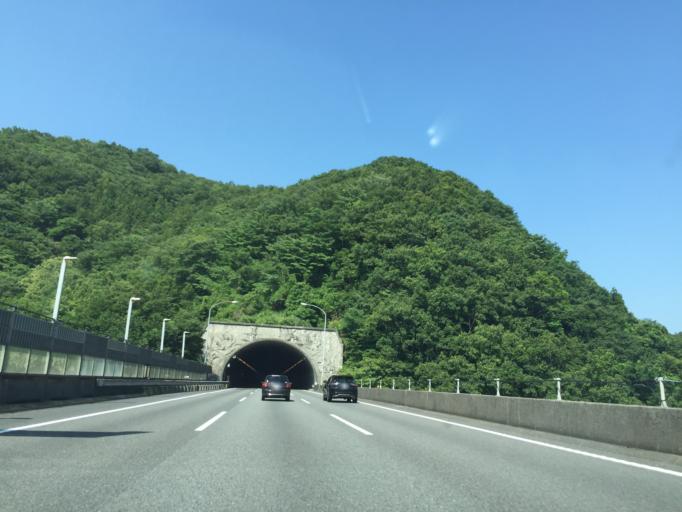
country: JP
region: Shizuoka
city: Gotemba
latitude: 35.3629
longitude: 139.0443
